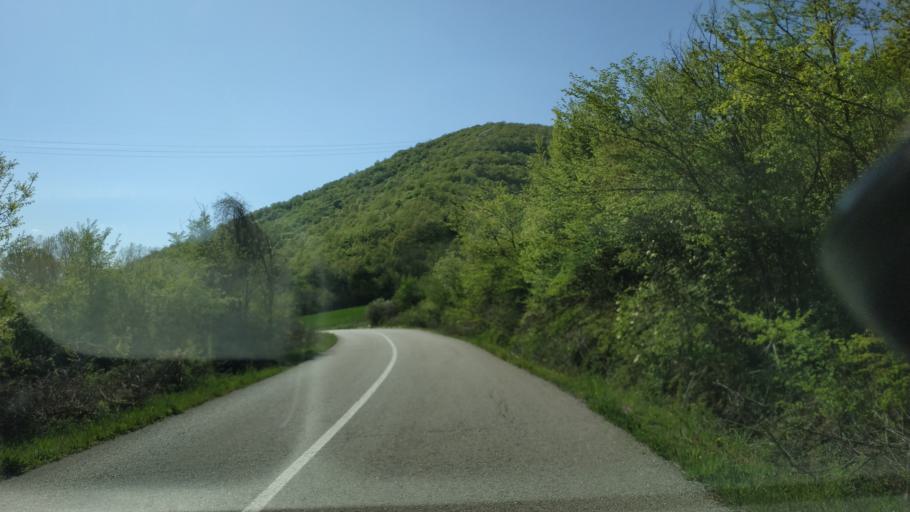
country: RS
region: Central Serbia
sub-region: Nisavski Okrug
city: Nis
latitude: 43.4184
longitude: 21.8453
